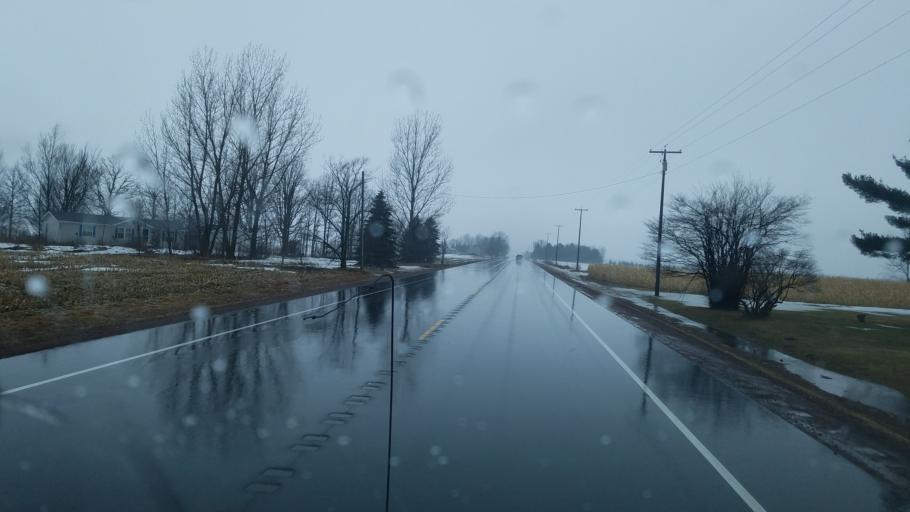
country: US
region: Wisconsin
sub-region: Marathon County
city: Spencer
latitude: 44.6563
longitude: -90.2828
